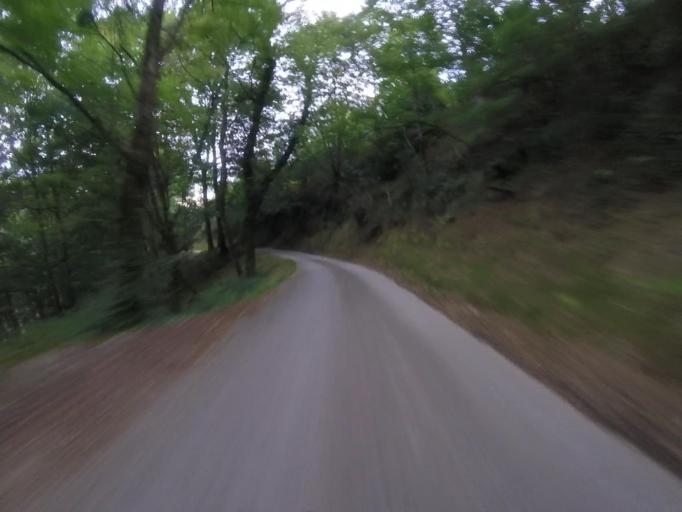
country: ES
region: Basque Country
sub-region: Provincia de Guipuzcoa
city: Errenteria
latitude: 43.2736
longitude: -1.8347
